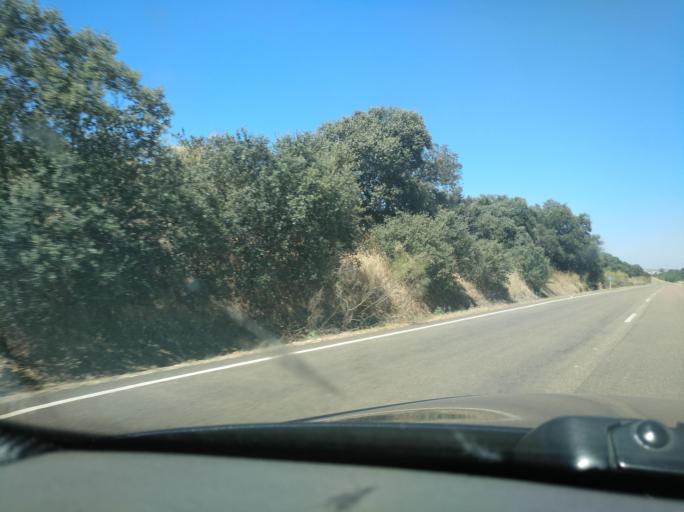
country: ES
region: Extremadura
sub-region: Provincia de Badajoz
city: Olivenza
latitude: 38.7143
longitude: -7.1930
